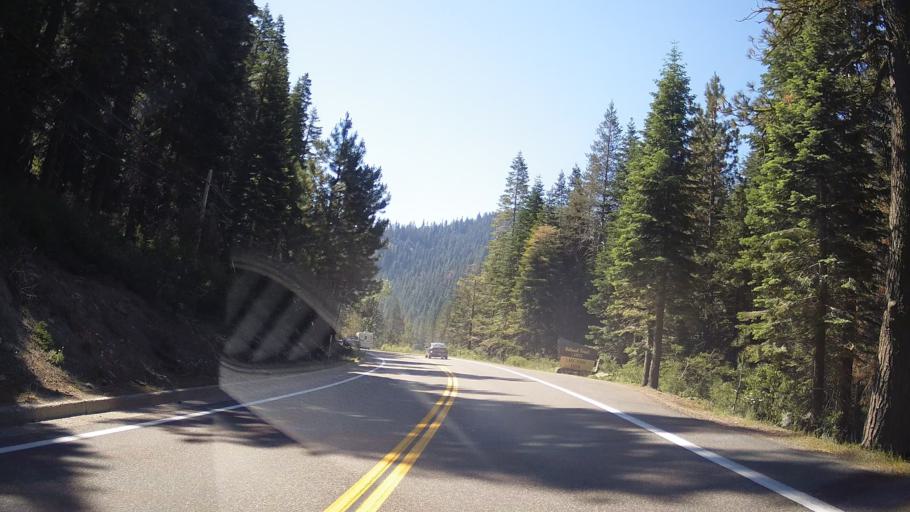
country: US
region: California
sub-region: Placer County
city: Sunnyside-Tahoe City
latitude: 39.1717
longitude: -120.1878
